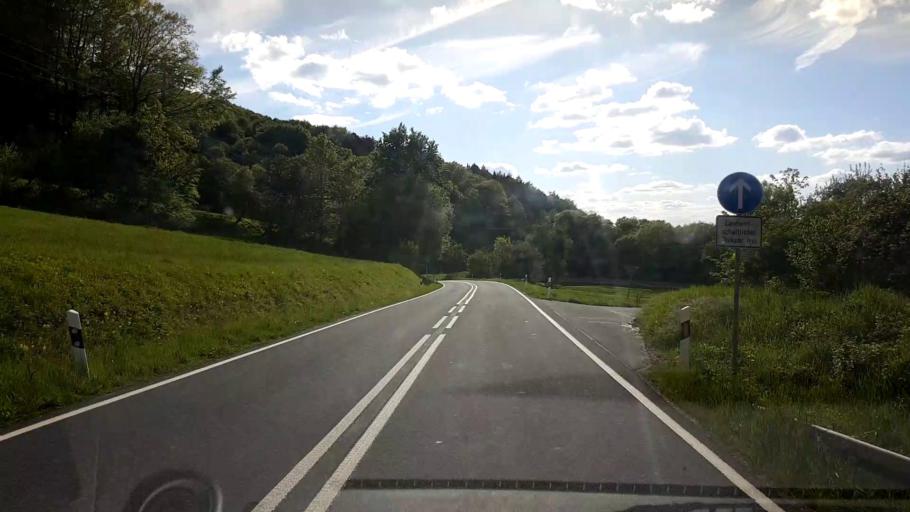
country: DE
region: Bavaria
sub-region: Upper Franconia
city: Poxdorf
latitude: 49.9757
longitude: 11.0968
